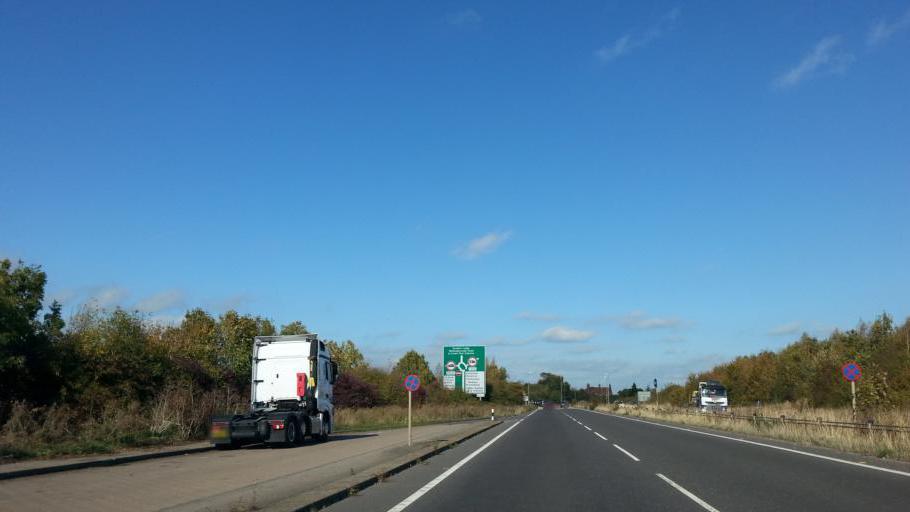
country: GB
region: England
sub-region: Northamptonshire
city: Higham Ferrers
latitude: 52.3064
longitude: -0.5840
